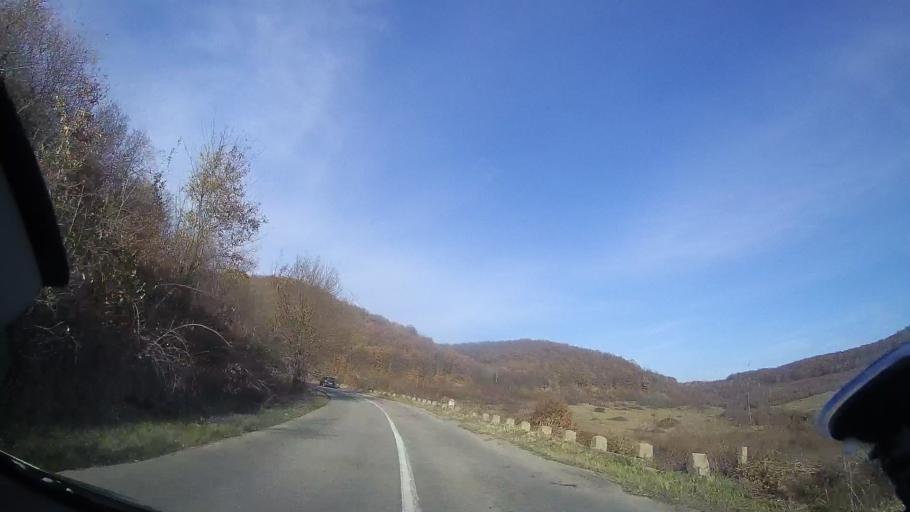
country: RO
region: Bihor
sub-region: Comuna Tileagd
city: Tileagd
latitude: 47.0928
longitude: 22.2360
